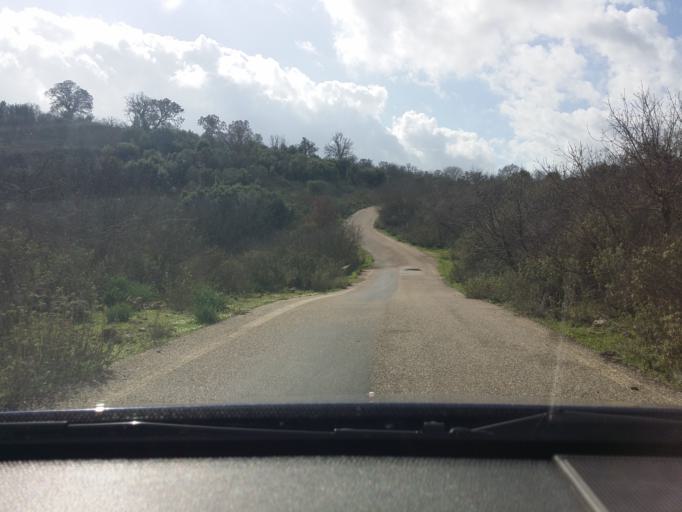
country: GR
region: West Greece
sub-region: Nomos Aitolias kai Akarnanias
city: Fitiai
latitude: 38.6430
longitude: 21.1969
